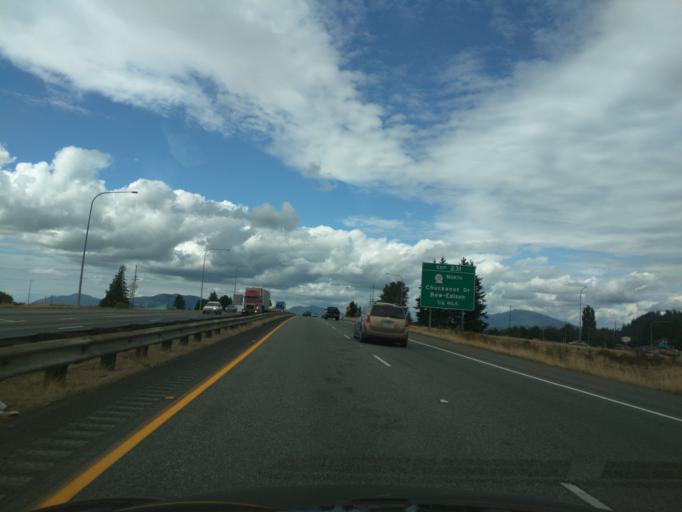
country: US
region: Washington
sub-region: Skagit County
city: Burlington
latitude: 48.4686
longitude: -122.3418
